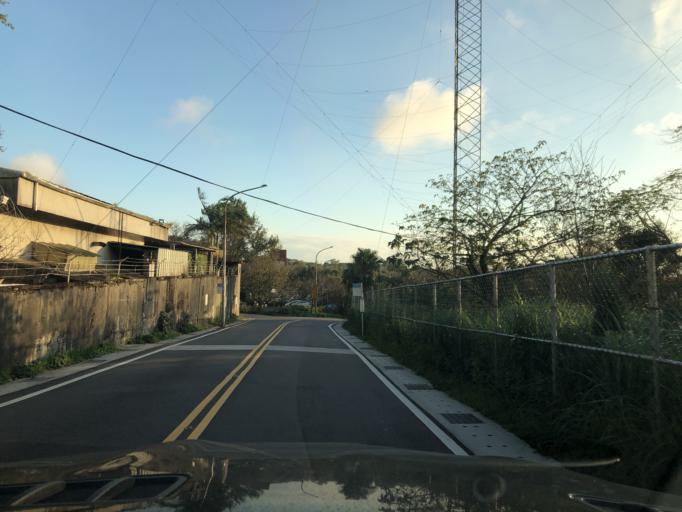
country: TW
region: Taipei
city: Taipei
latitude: 25.1444
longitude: 121.5575
